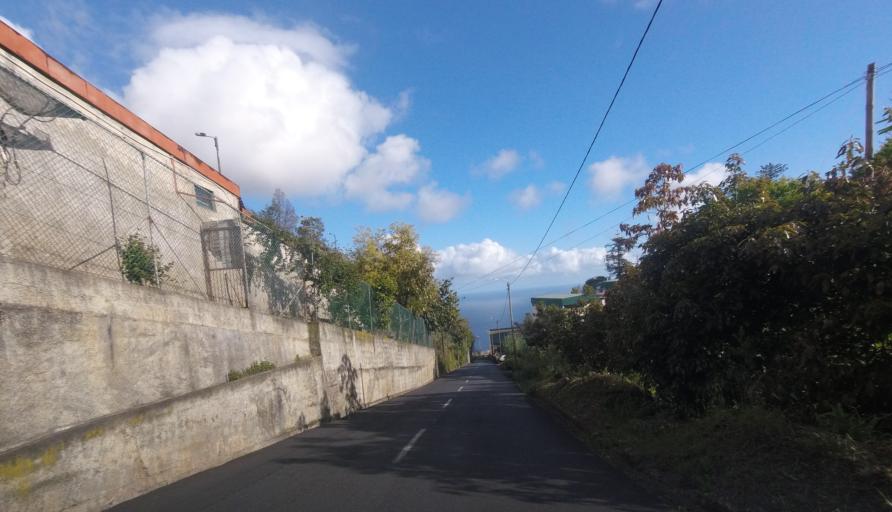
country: PT
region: Madeira
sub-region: Funchal
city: Nossa Senhora do Monte
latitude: 32.6691
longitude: -16.9027
